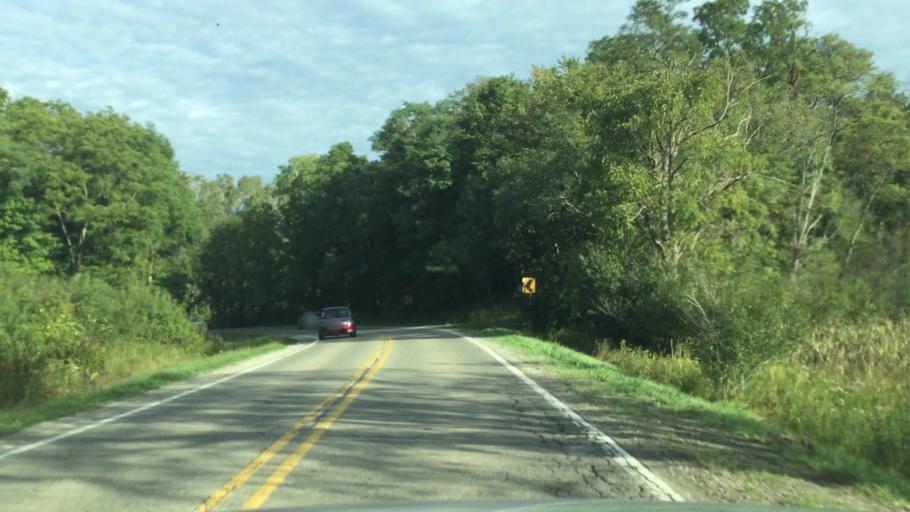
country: US
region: Michigan
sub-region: Livingston County
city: Brighton
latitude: 42.4892
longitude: -83.8528
